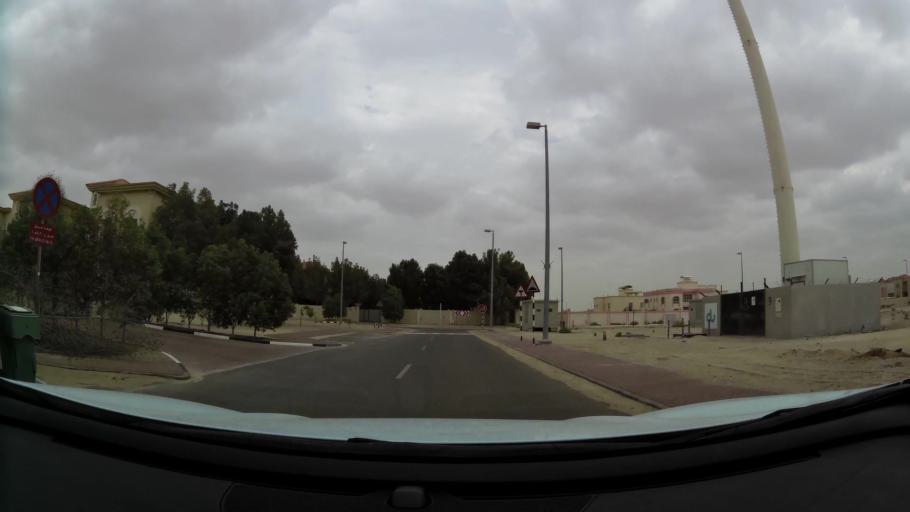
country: AE
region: Abu Dhabi
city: Abu Dhabi
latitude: 24.3753
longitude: 54.6408
